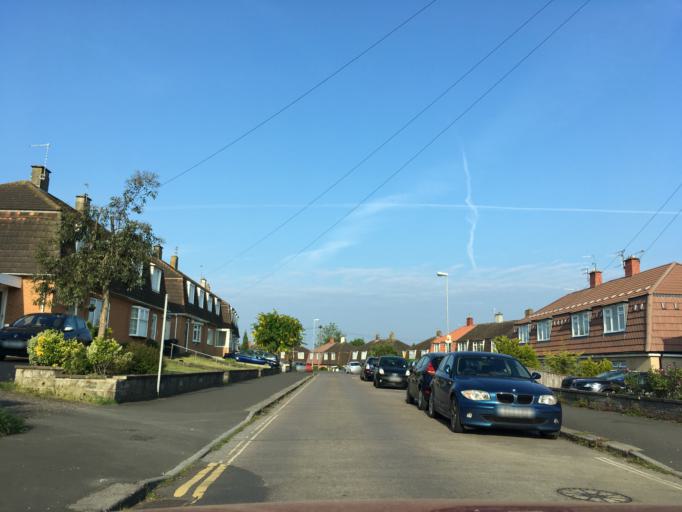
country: GB
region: England
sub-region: Bristol
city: Bristol
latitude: 51.5017
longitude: -2.5879
